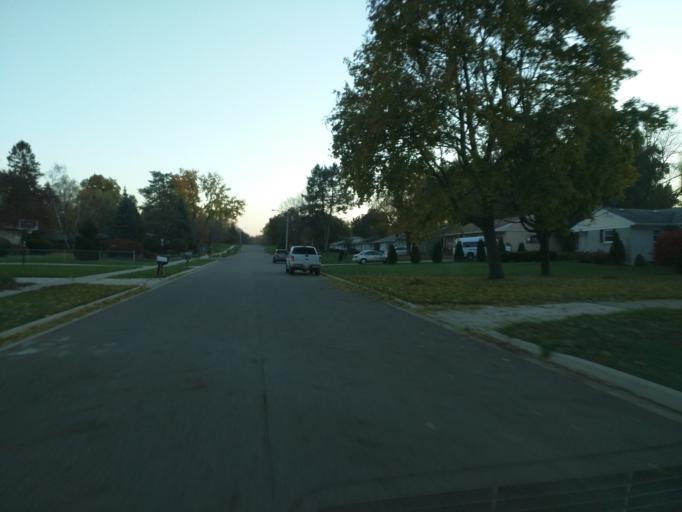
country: US
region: Michigan
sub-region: Eaton County
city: Waverly
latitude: 42.7325
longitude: -84.6086
